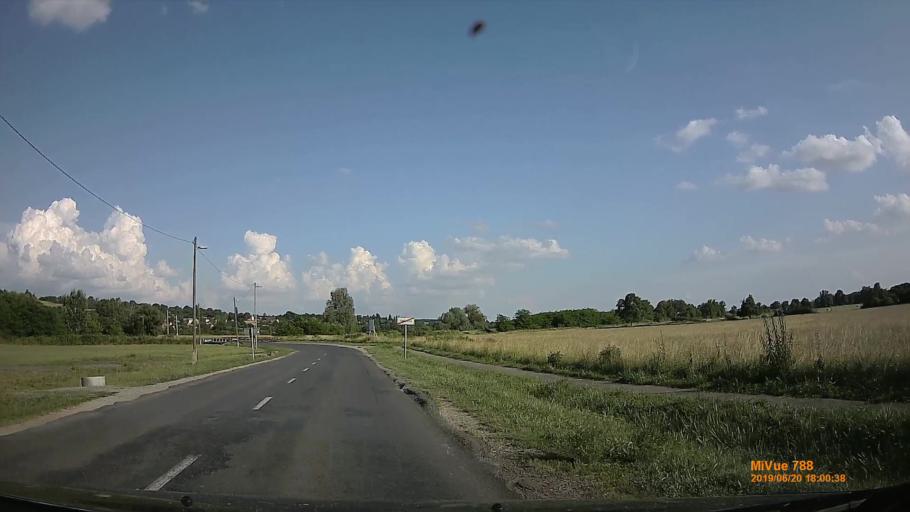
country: HU
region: Baranya
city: Buekkoesd
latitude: 46.0873
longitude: 17.9829
